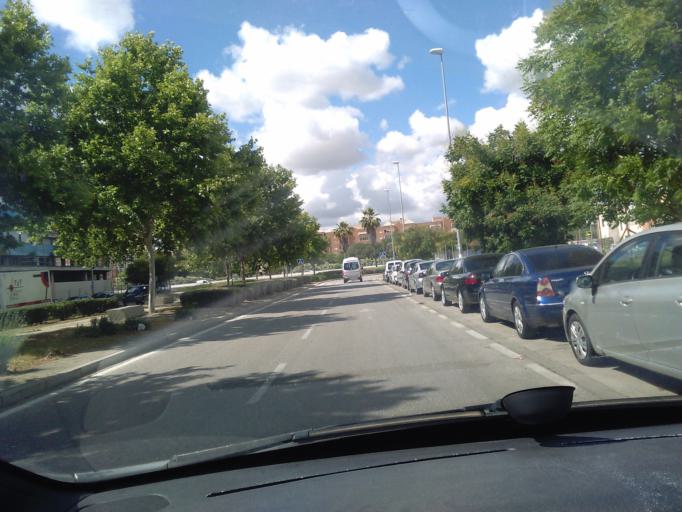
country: ES
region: Andalusia
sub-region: Provincia de Sevilla
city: Sevilla
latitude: 37.3847
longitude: -5.9190
